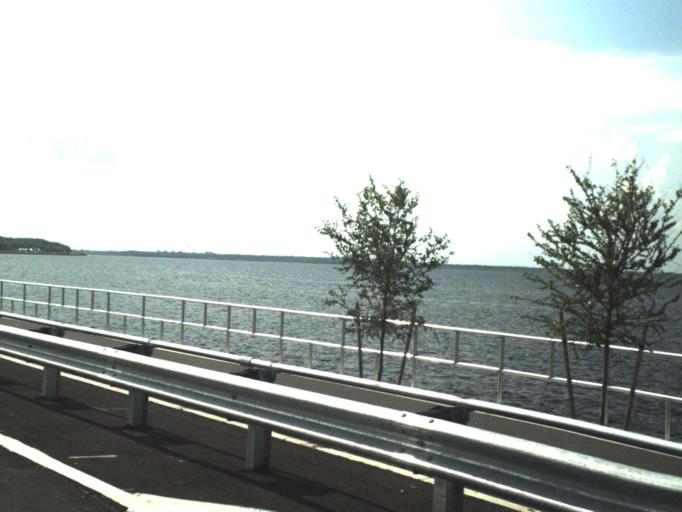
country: US
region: Florida
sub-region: Seminole County
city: Sanford
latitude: 28.8162
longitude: -81.2794
